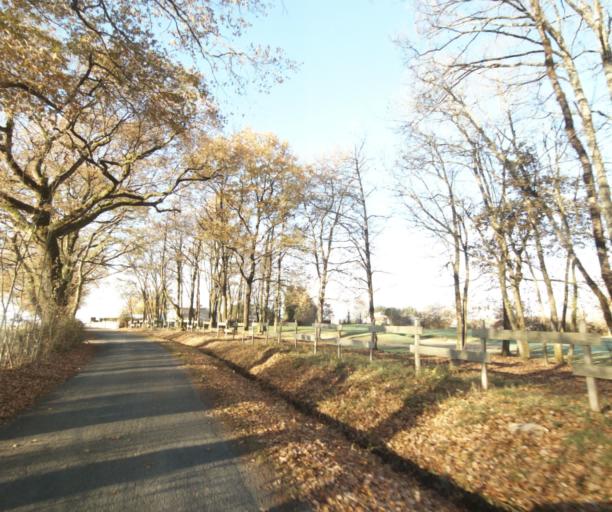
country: FR
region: Poitou-Charentes
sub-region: Departement de la Charente-Maritime
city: Fontcouverte
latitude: 45.7624
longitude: -0.6062
